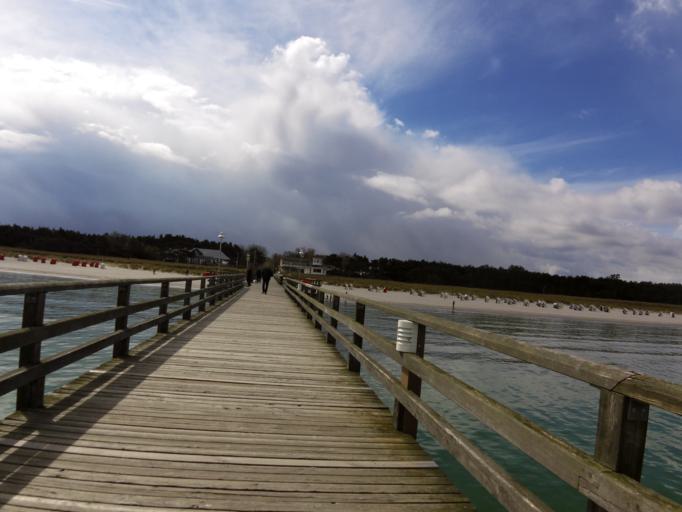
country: DE
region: Mecklenburg-Vorpommern
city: Ostseebad Prerow
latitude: 54.4545
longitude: 12.5703
